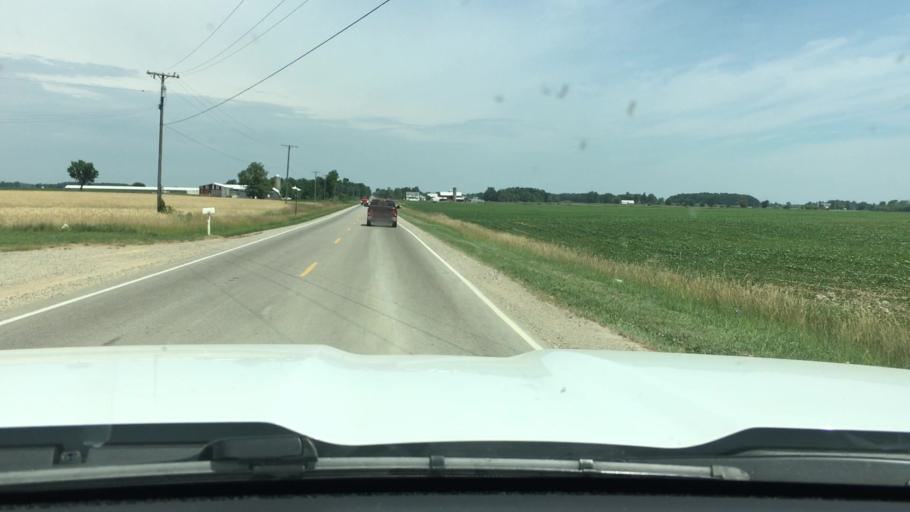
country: US
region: Michigan
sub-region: Sanilac County
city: Brown City
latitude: 43.2854
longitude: -82.9828
